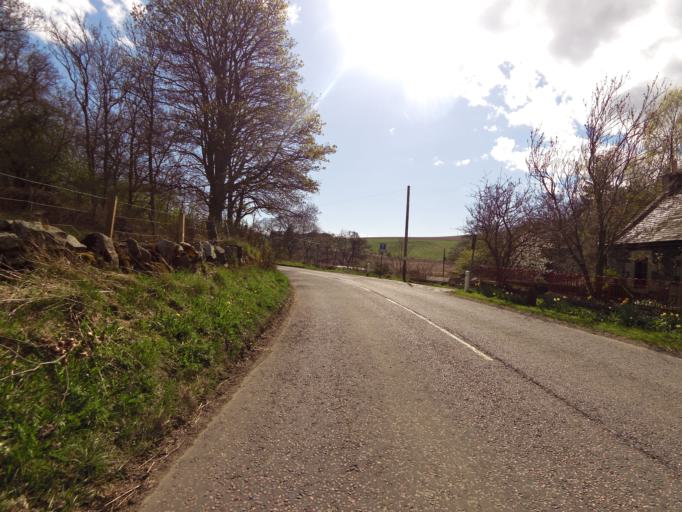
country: GB
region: Scotland
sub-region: Fife
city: Auchtermuchty
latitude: 56.3053
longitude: -3.2407
